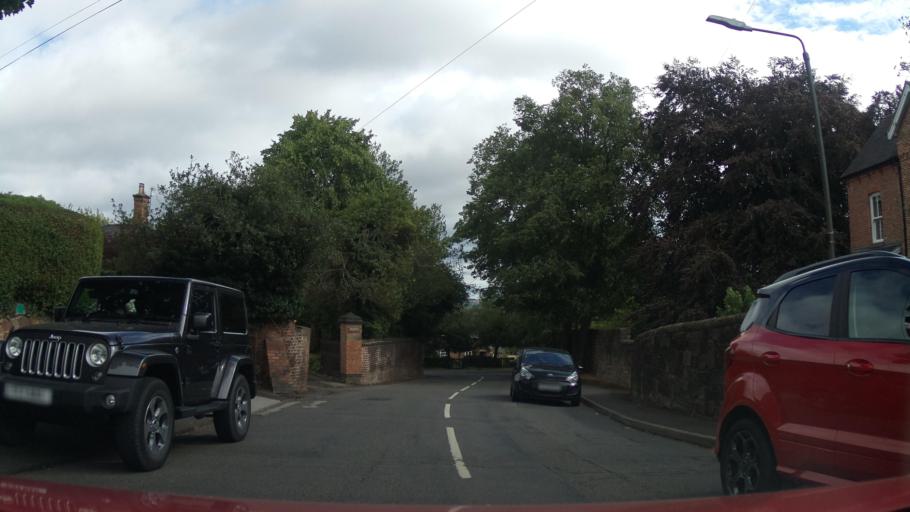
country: GB
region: England
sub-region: Derbyshire
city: Ilkeston
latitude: 52.9381
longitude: -1.3086
